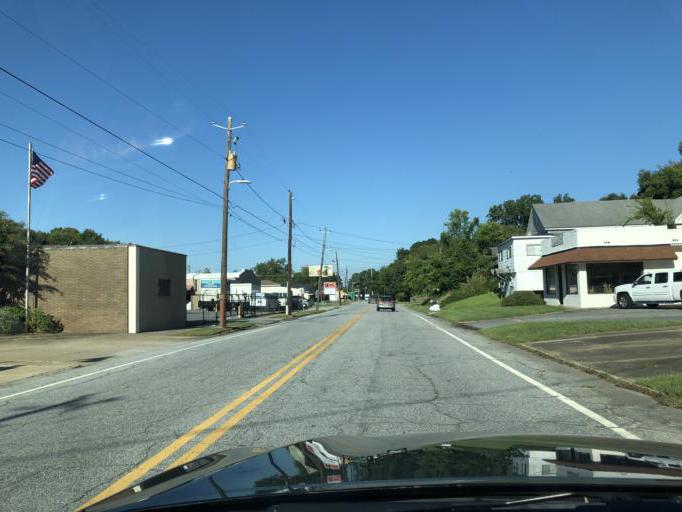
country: US
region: Georgia
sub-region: Muscogee County
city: Columbus
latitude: 32.4777
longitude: -84.9763
